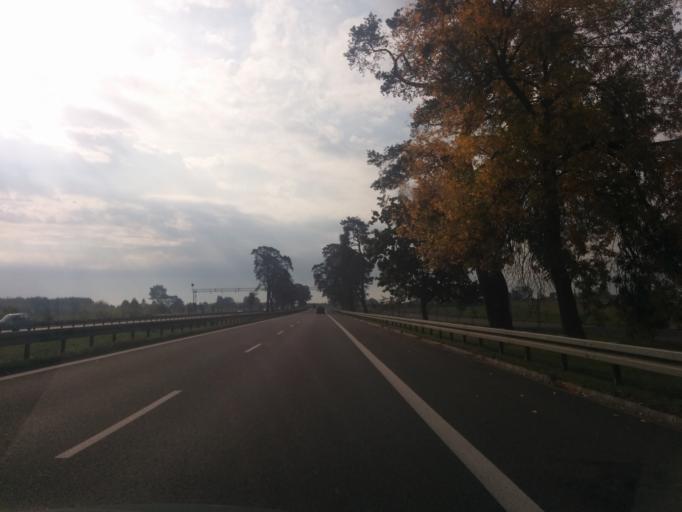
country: PL
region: Masovian Voivodeship
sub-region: Powiat bialobrzeski
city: Stara Blotnica
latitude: 51.5918
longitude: 20.9943
